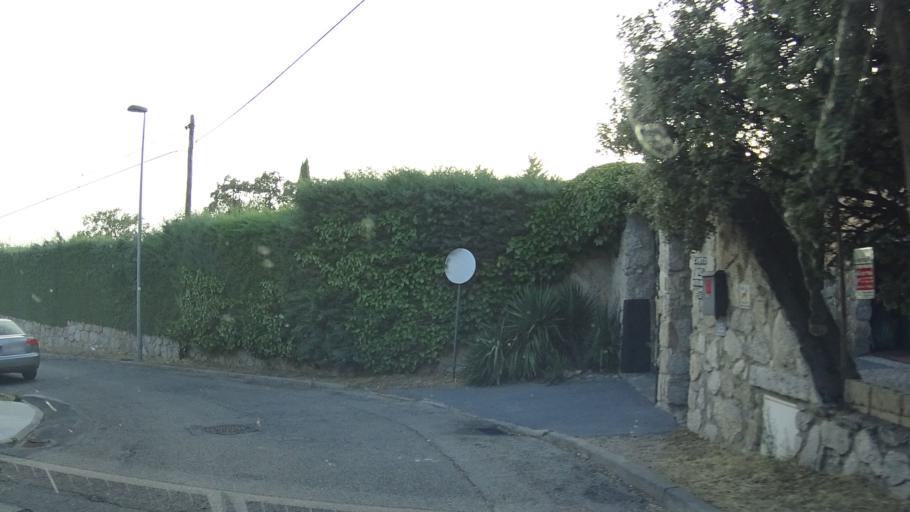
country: ES
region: Madrid
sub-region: Provincia de Madrid
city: Torrelodones
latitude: 40.5887
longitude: -3.9464
